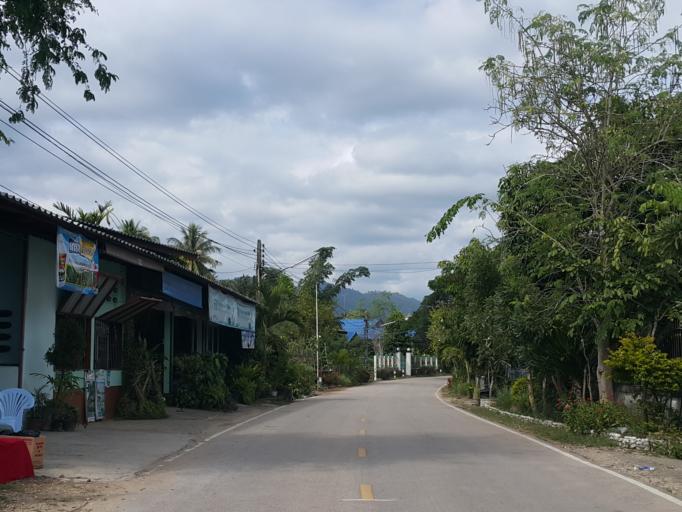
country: TH
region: Lampang
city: Chae Hom
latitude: 18.5582
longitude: 99.4579
